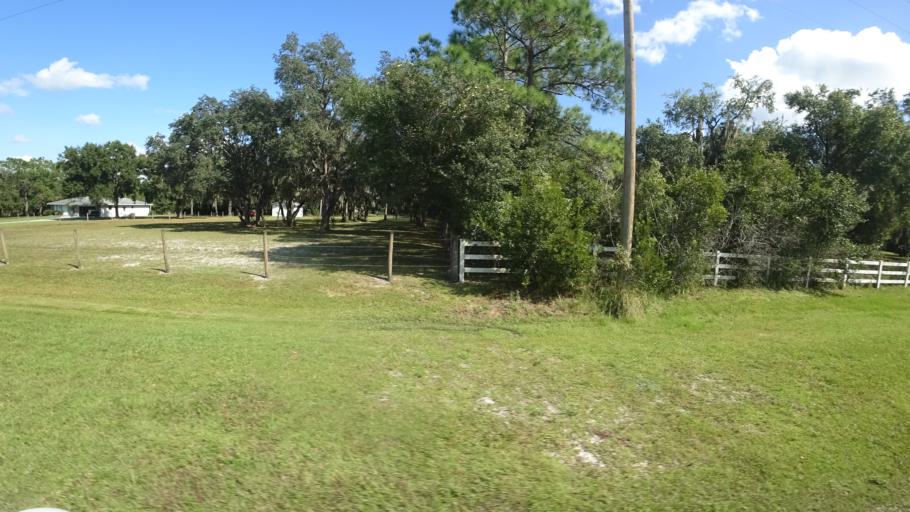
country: US
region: Florida
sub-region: Sarasota County
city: The Meadows
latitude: 27.4727
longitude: -82.3156
